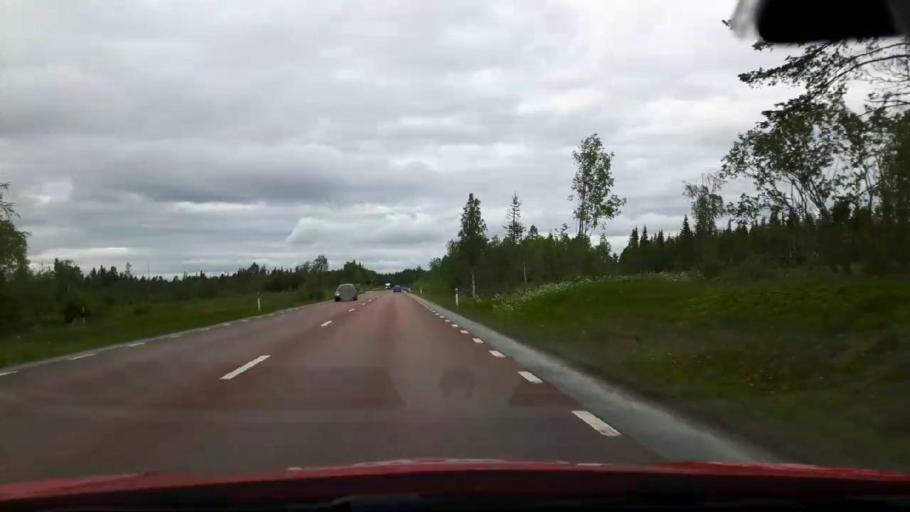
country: SE
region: Jaemtland
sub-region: Bergs Kommun
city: Hoverberg
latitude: 62.9334
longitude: 14.5392
